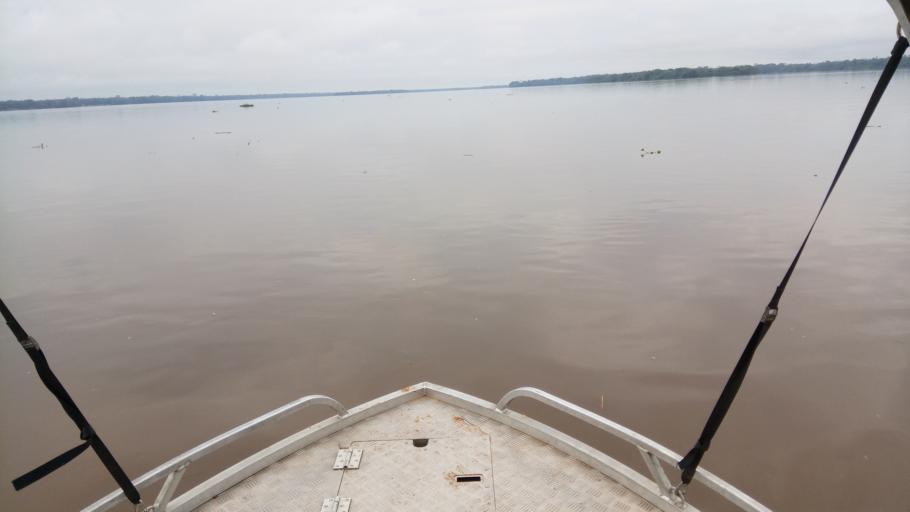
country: CD
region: Eastern Province
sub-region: Sous-Region de la Tshopo
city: Yangambi
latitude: 0.7519
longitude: 24.4020
